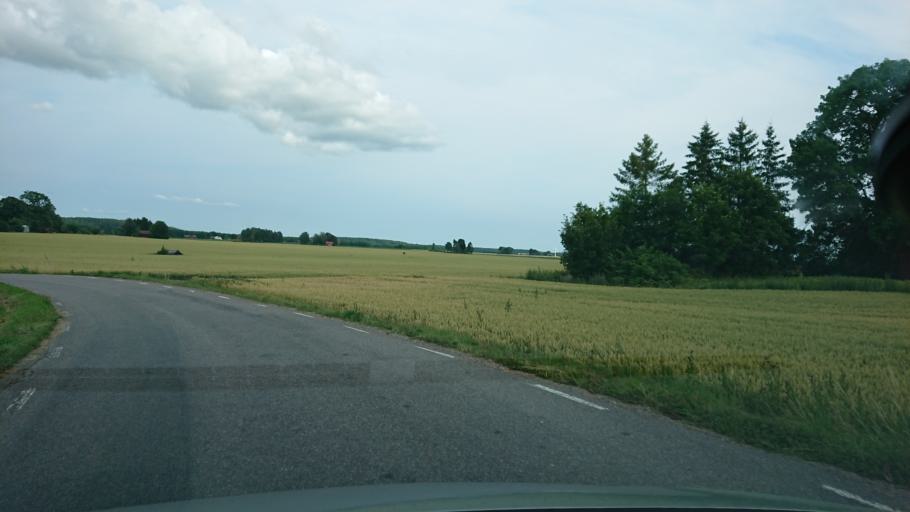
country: SE
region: Uppsala
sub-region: Osthammars Kommun
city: Bjorklinge
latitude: 59.9892
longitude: 17.5320
